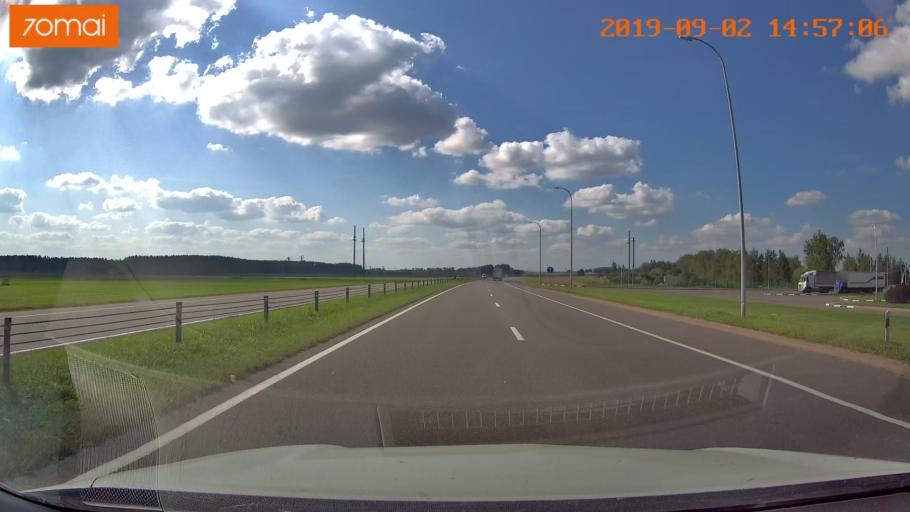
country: BY
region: Mogilev
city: Buynichy
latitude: 53.9658
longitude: 30.1713
